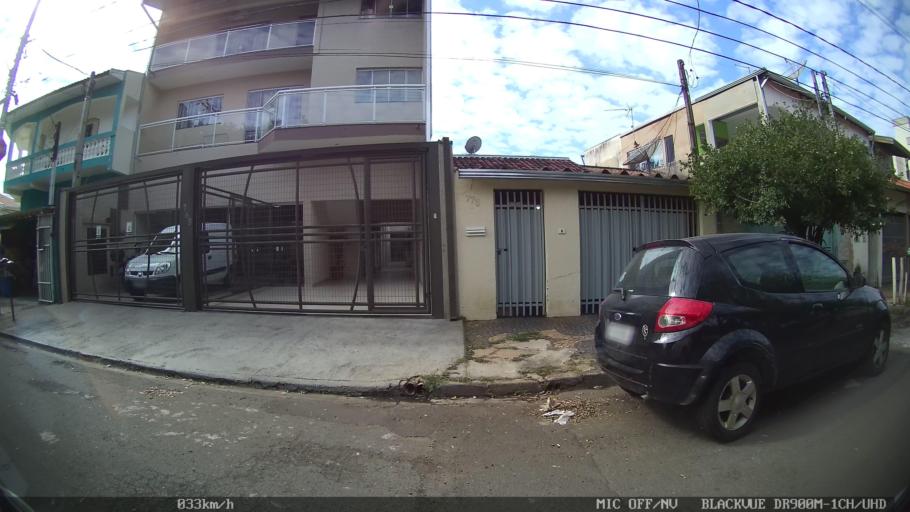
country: BR
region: Sao Paulo
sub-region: Santa Barbara D'Oeste
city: Santa Barbara d'Oeste
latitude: -22.7696
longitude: -47.3897
